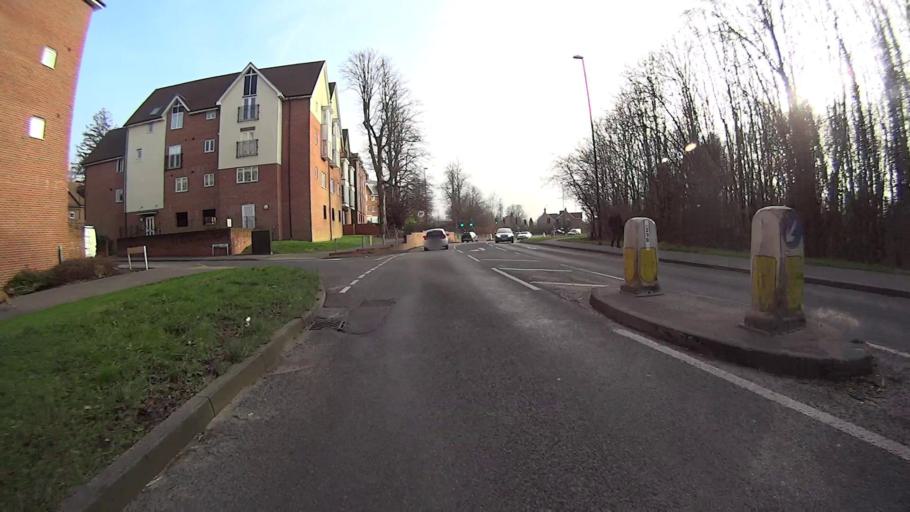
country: GB
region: England
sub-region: West Sussex
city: Maidenbower
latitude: 51.1128
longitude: -0.1466
